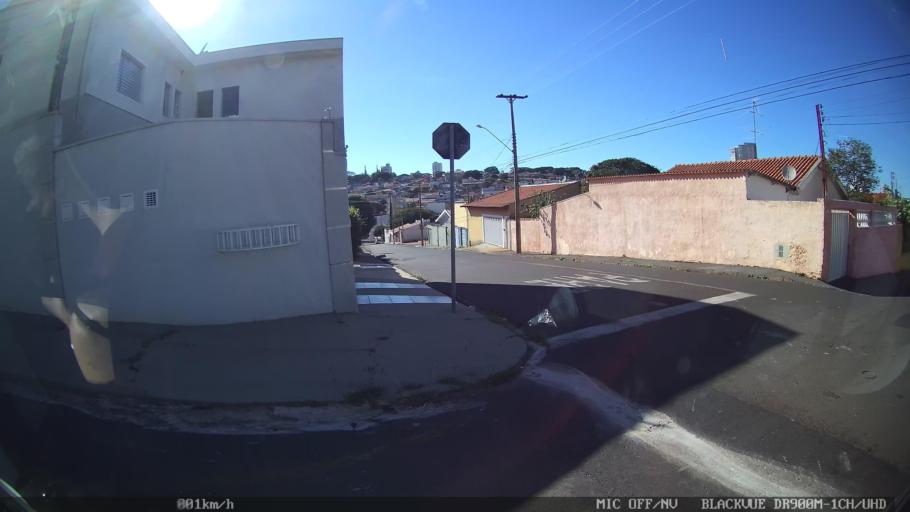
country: BR
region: Sao Paulo
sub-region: Franca
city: Franca
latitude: -20.5438
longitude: -47.4100
